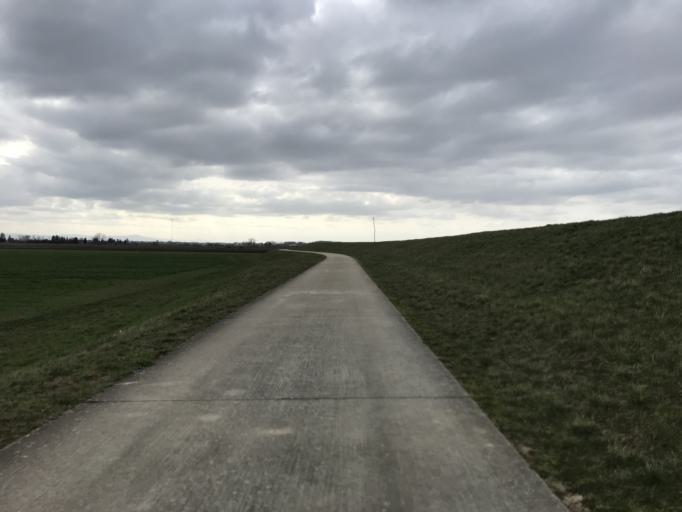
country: DE
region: Rheinland-Pfalz
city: Nierstein
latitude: 49.8834
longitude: 8.3626
